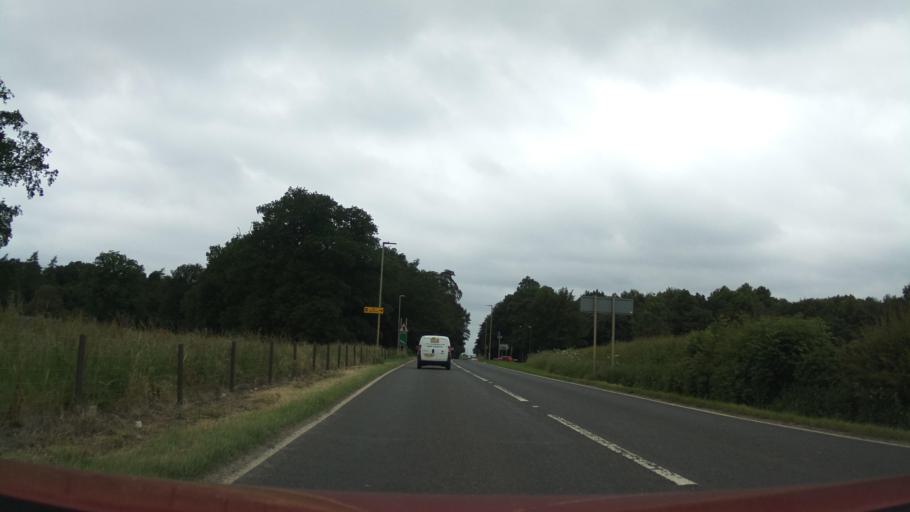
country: GB
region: England
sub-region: Nottinghamshire
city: East Leake
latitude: 52.8142
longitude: -1.1776
